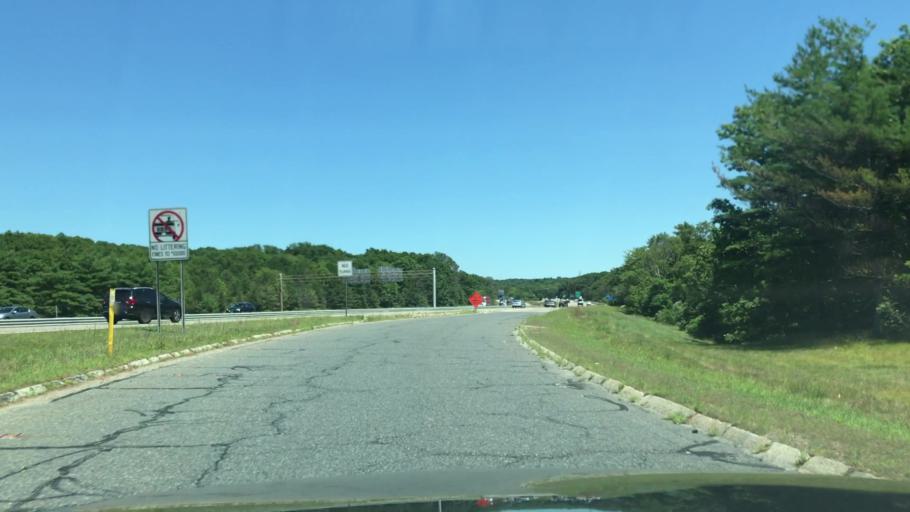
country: US
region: Massachusetts
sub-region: Bristol County
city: North Seekonk
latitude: 41.9031
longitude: -71.3526
